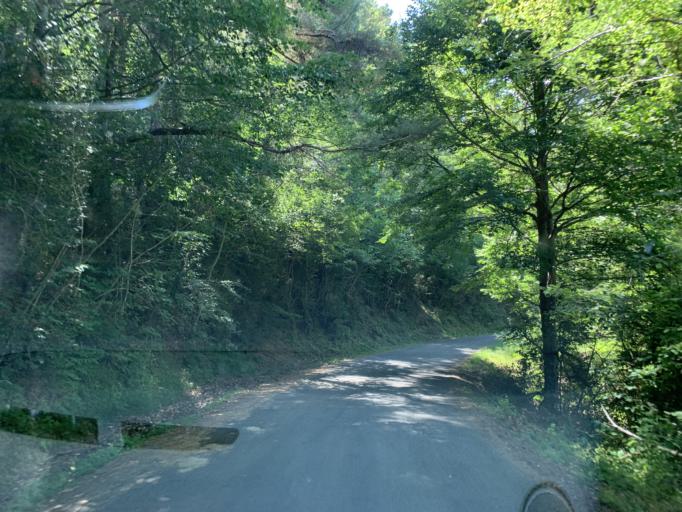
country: ES
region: Aragon
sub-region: Provincia de Huesca
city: Hoz de Jaca
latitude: 42.6974
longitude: -0.3080
